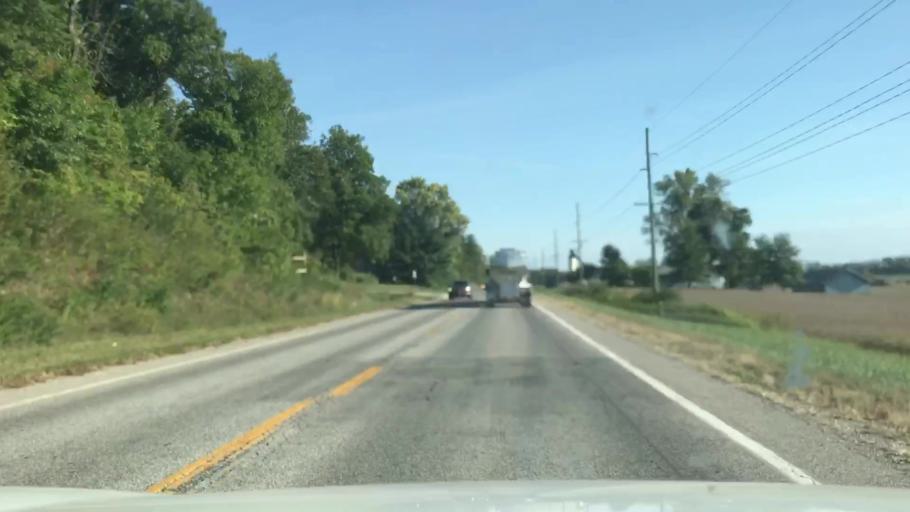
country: US
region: Illinois
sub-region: Adams County
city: Quincy
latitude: 39.8532
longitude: -91.3822
